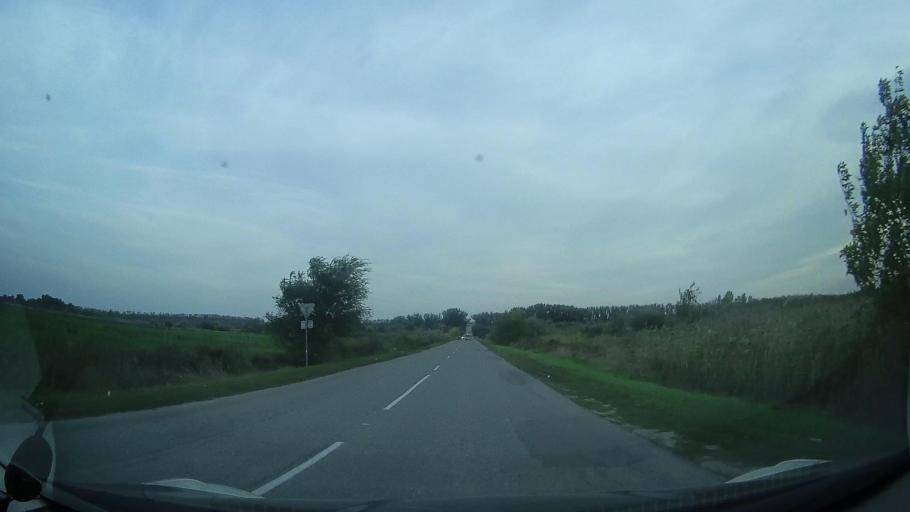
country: RU
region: Rostov
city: Ol'ginskaya
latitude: 47.1304
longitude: 39.9624
